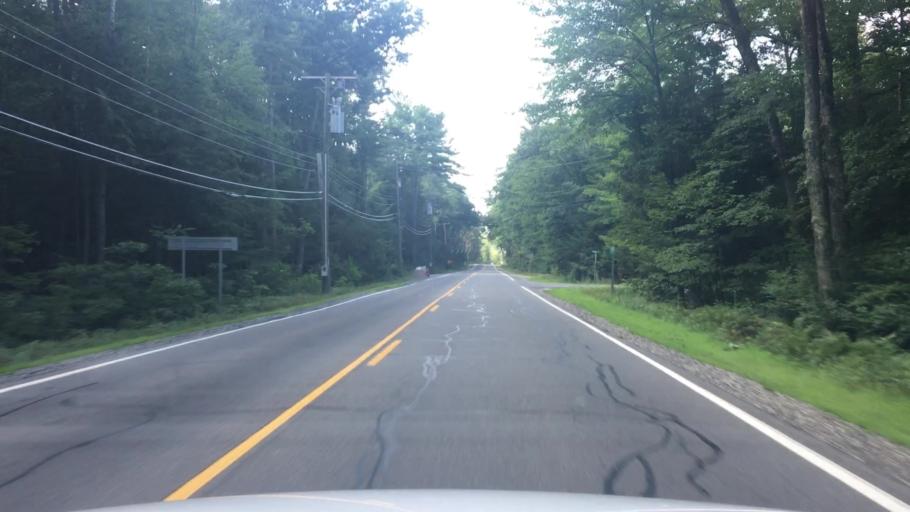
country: US
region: New Hampshire
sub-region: Rockingham County
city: Auburn
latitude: 42.9817
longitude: -71.3709
